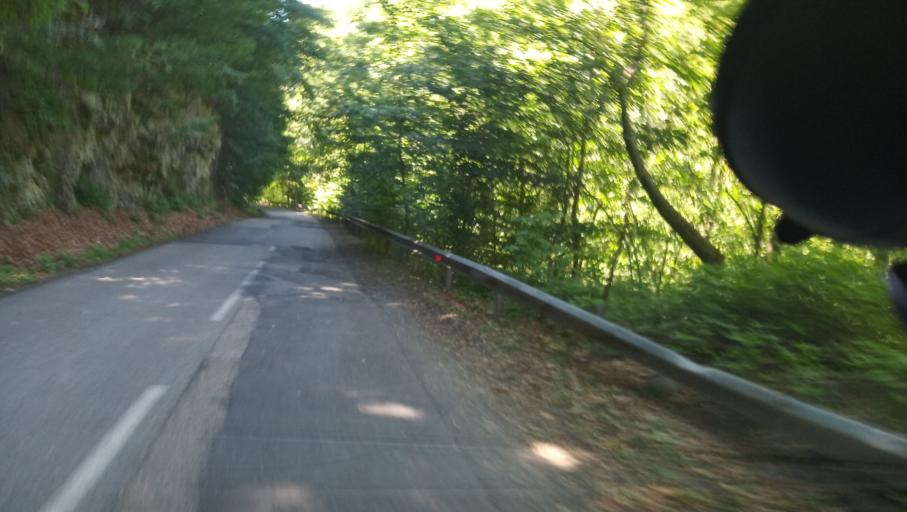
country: RO
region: Mehedinti
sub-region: Comuna Podeni
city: Podeni
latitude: 44.9907
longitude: 22.5153
